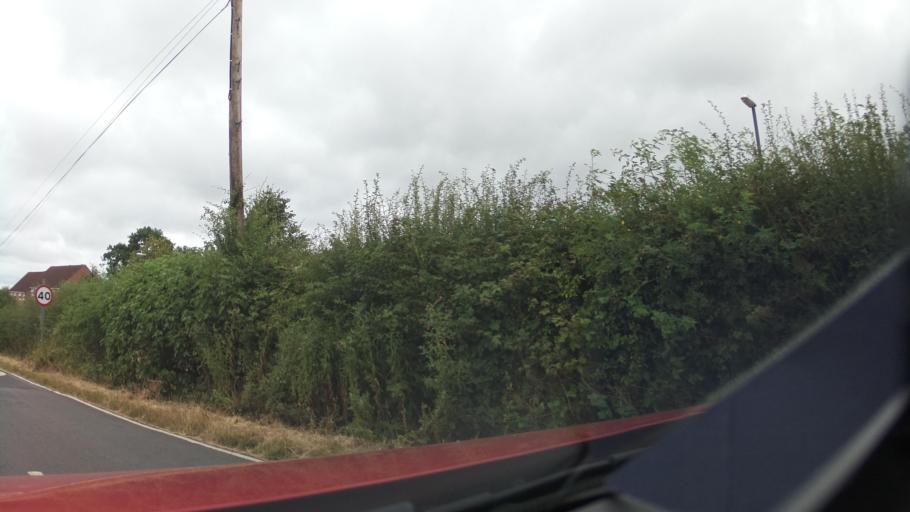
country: GB
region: England
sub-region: Derbyshire
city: Findern
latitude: 52.8927
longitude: -1.5148
